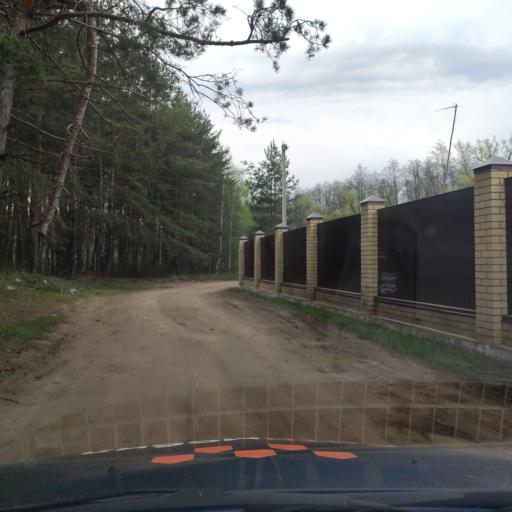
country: RU
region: Voronezj
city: Podgornoye
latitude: 51.8680
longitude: 39.1692
